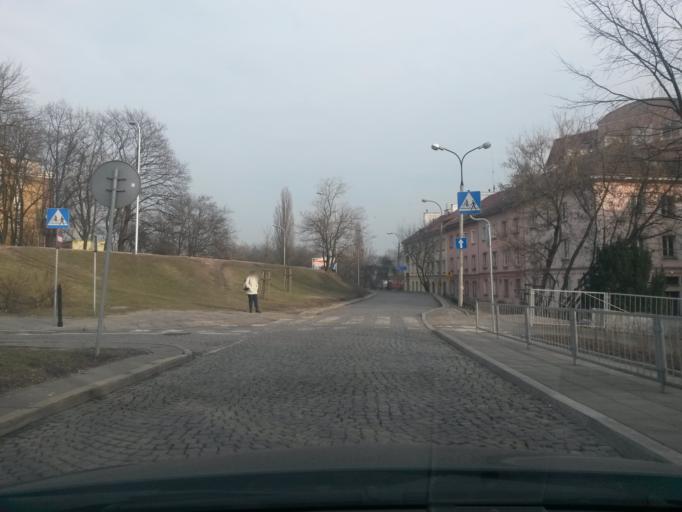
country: PL
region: Masovian Voivodeship
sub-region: Warszawa
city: Srodmiescie
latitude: 52.2468
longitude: 21.0174
